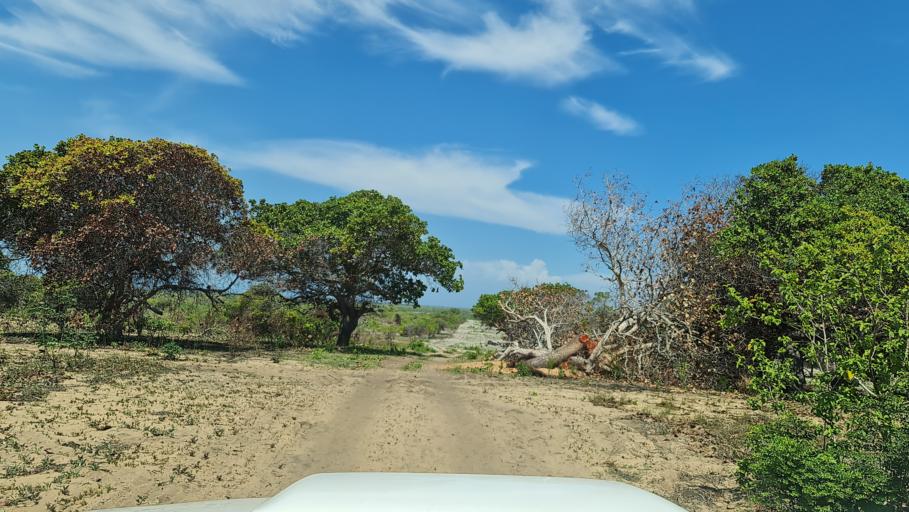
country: MZ
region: Nampula
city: Ilha de Mocambique
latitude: -15.1979
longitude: 40.6127
